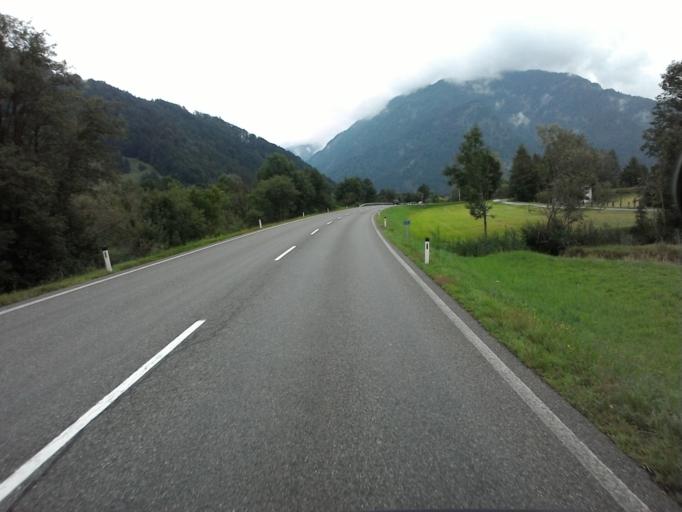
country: AT
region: Tyrol
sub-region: Politischer Bezirk Kitzbuhel
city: Kirchdorf in Tirol
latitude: 47.5684
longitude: 12.4682
